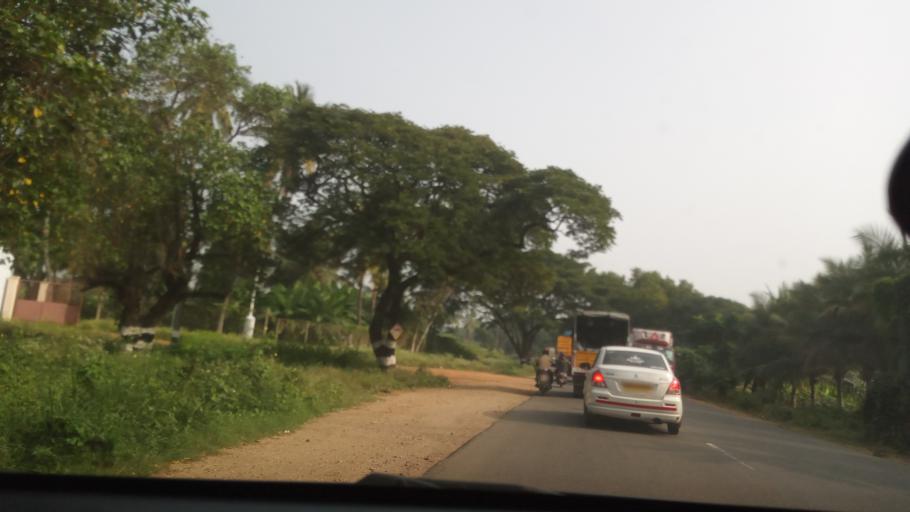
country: IN
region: Tamil Nadu
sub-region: Coimbatore
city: Annur
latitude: 11.1851
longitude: 77.0625
